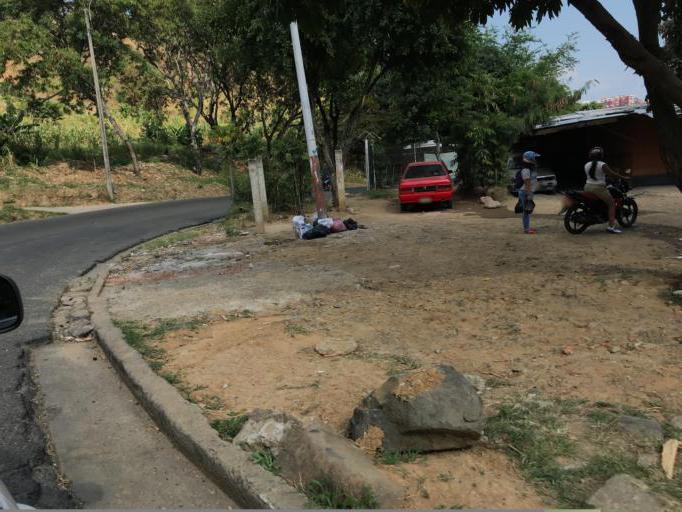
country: CO
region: Valle del Cauca
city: Cali
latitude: 3.4510
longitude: -76.5618
